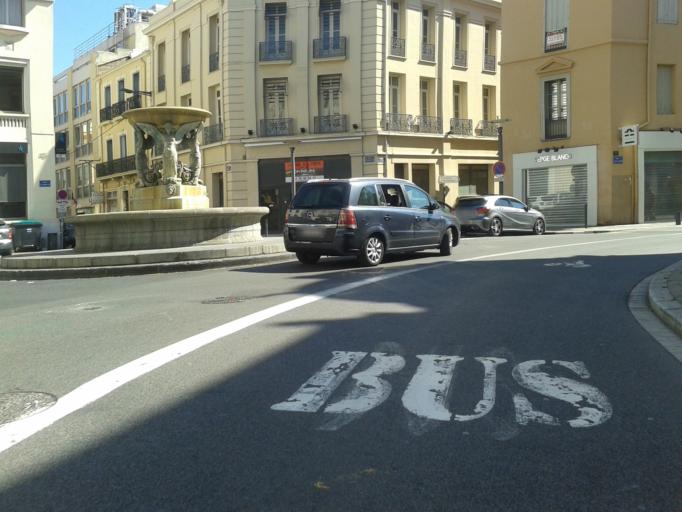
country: FR
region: Languedoc-Roussillon
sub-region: Departement des Pyrenees-Orientales
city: Perpignan
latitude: 42.6989
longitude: 2.8905
